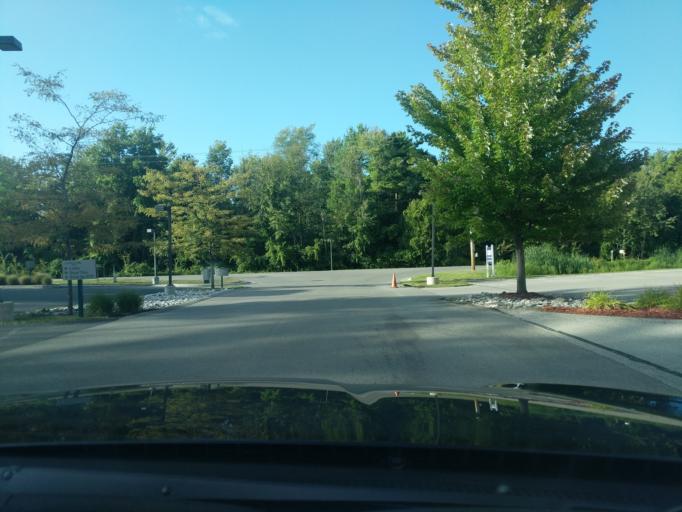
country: US
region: Michigan
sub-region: Leelanau County
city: Leland
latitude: 44.9699
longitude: -85.6501
